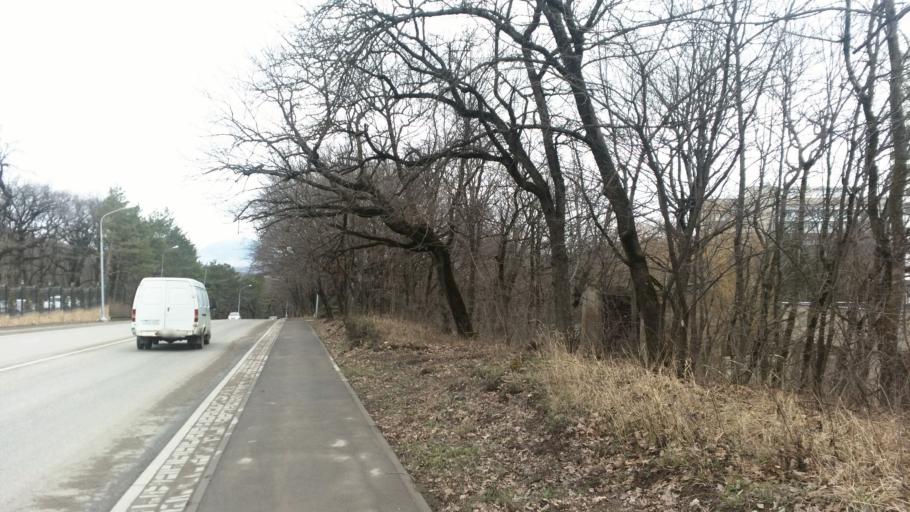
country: RU
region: Stavropol'skiy
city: Zheleznovodsk
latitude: 44.1347
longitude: 43.0193
